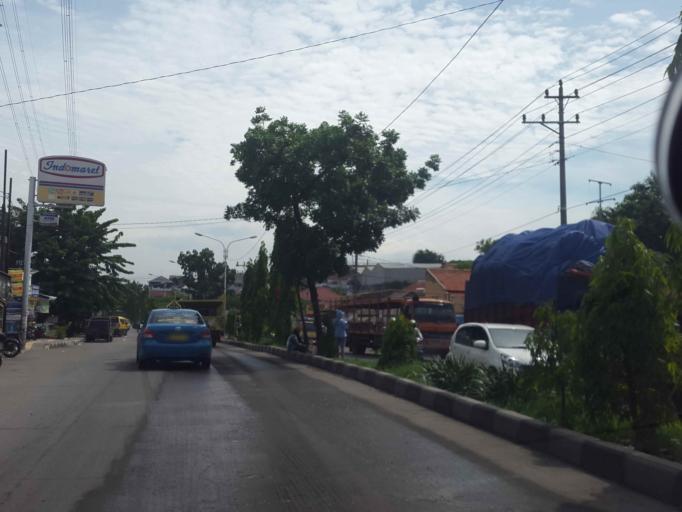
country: ID
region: Central Java
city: Semarang
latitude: -6.9882
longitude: 110.3668
